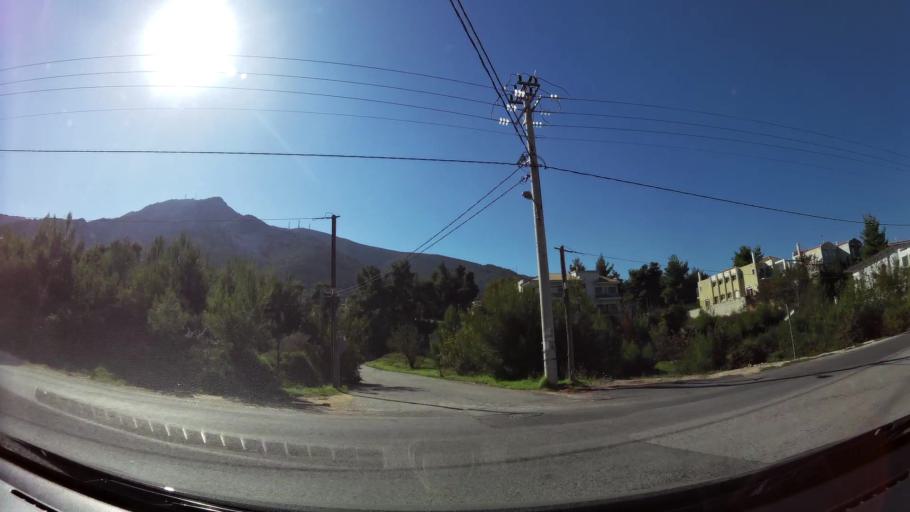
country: GR
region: Attica
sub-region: Nomarchia Anatolikis Attikis
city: Dionysos
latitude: 38.0970
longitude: 23.8892
